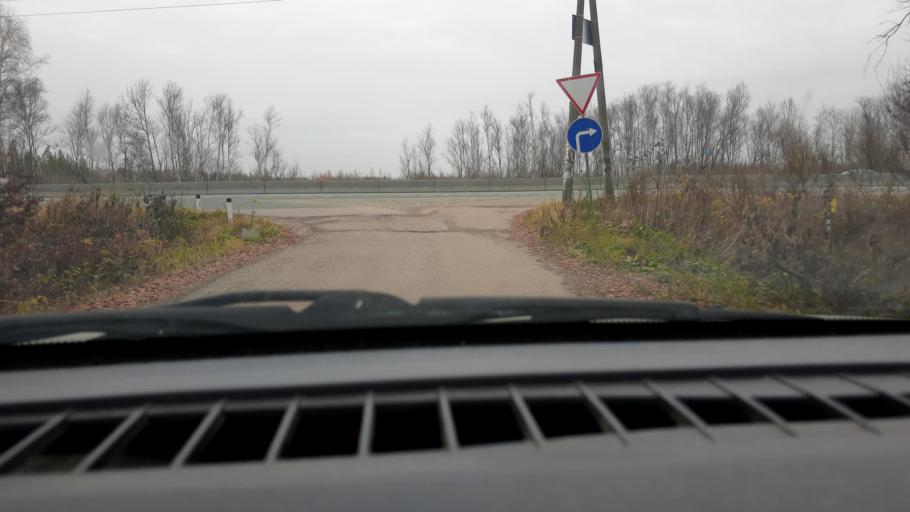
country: RU
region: Nizjnij Novgorod
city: Gorbatovka
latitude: 56.3075
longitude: 43.7249
